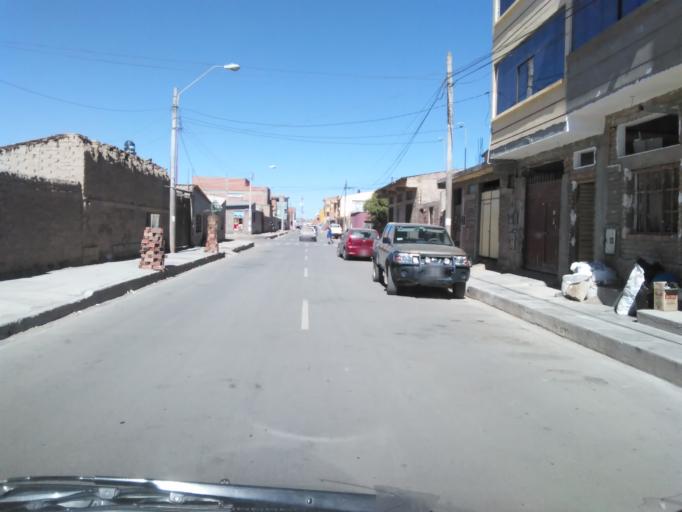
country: BO
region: Oruro
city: Oruro
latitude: -17.9659
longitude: -67.0991
